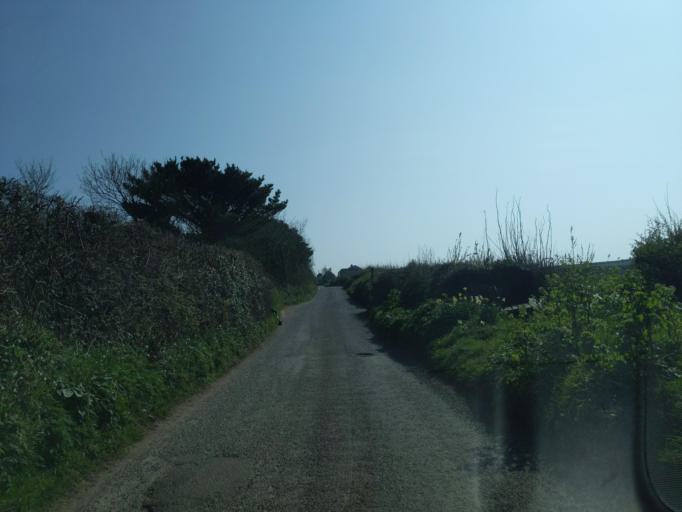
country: GB
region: England
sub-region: Devon
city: Dartmouth
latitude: 50.3157
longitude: -3.6325
